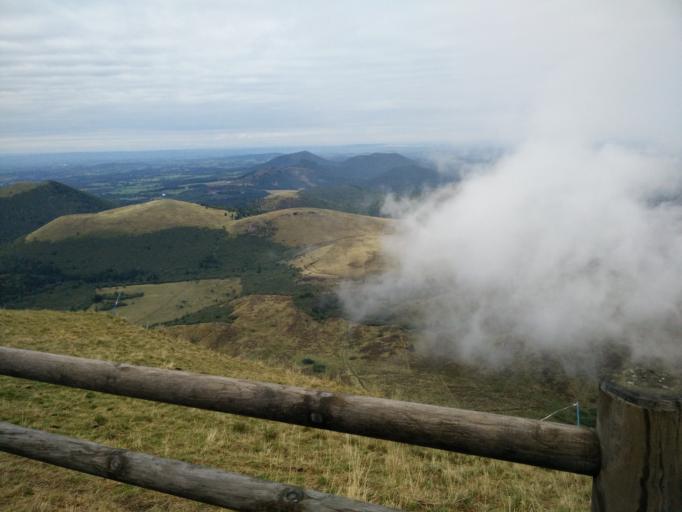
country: FR
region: Auvergne
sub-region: Departement du Puy-de-Dome
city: Orcines
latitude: 45.7730
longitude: 2.9647
